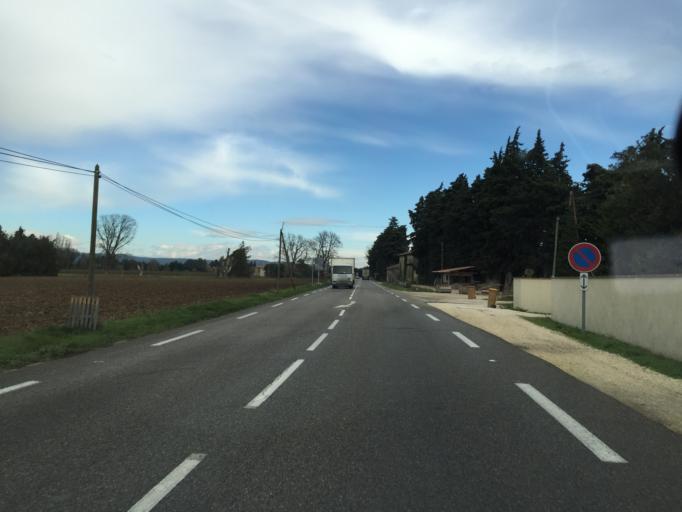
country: FR
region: Provence-Alpes-Cote d'Azur
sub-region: Departement du Vaucluse
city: L'Isle-sur-la-Sorgue
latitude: 43.8739
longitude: 5.0618
